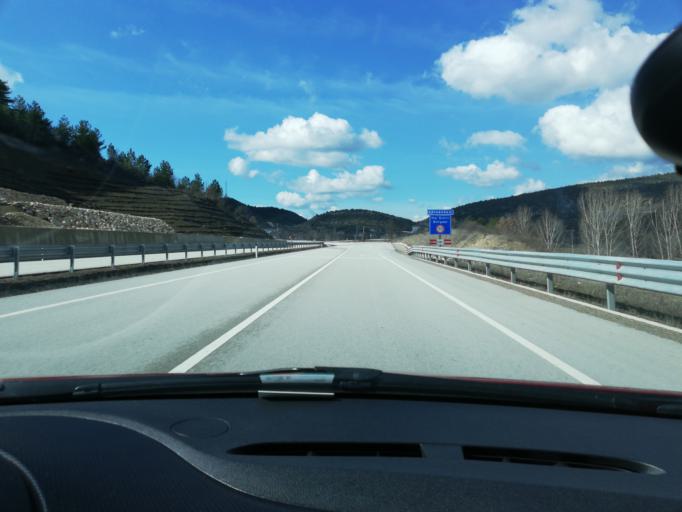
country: TR
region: Kastamonu
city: Igdir
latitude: 41.2314
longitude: 33.0387
